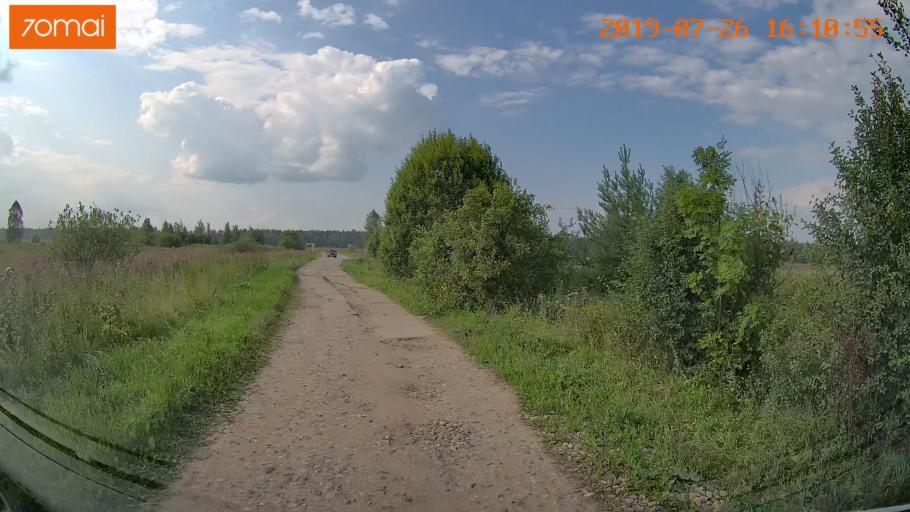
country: RU
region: Ivanovo
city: Bogorodskoye
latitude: 57.0645
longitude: 41.0619
